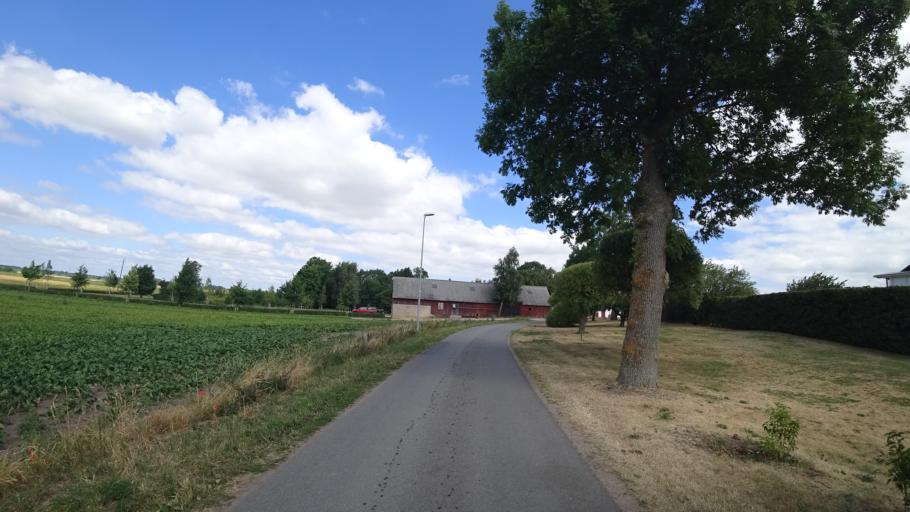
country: SE
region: Skane
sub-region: Kristianstads Kommun
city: Ahus
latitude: 55.9817
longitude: 14.2659
